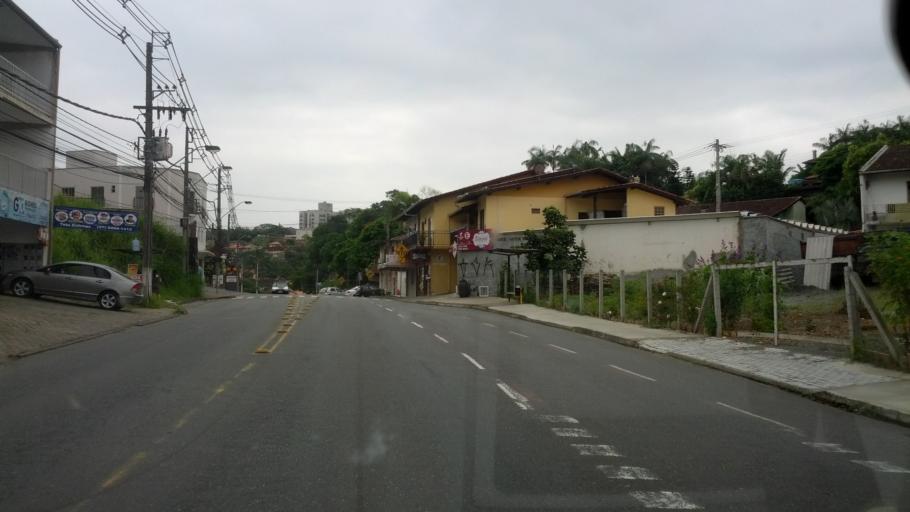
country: BR
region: Santa Catarina
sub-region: Blumenau
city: Blumenau
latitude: -26.9176
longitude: -49.1155
